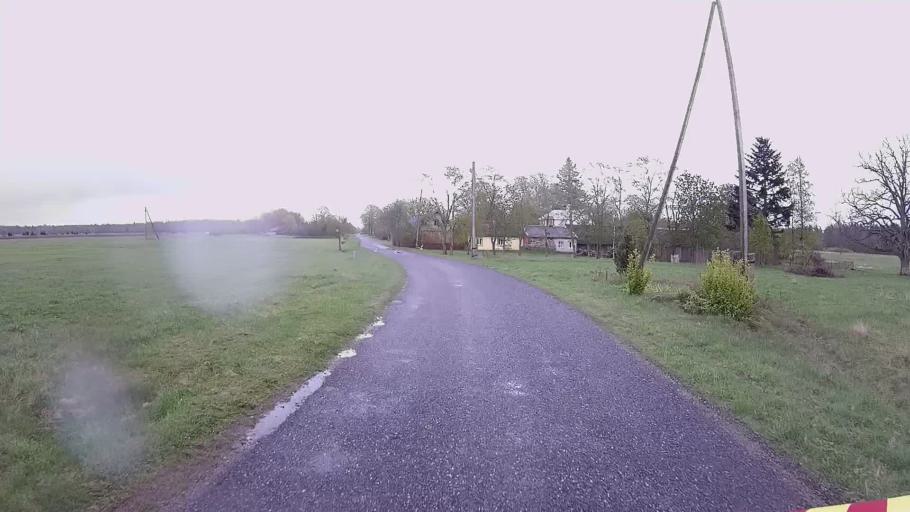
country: EE
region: Hiiumaa
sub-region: Kaerdla linn
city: Kardla
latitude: 58.6977
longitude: 22.5380
